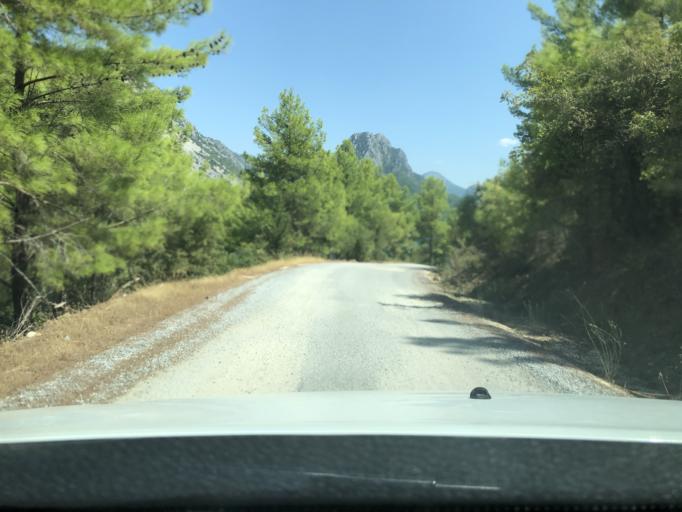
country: TR
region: Antalya
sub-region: Manavgat
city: Manavgat
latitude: 36.9109
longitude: 31.5493
